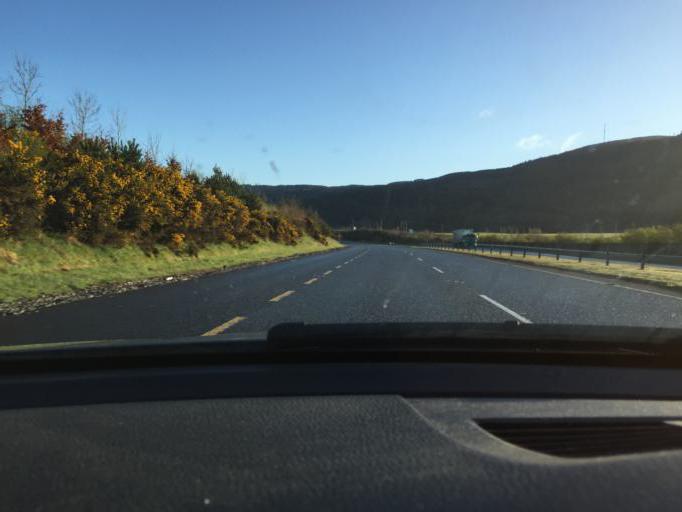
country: IE
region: Leinster
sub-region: Lu
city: Dundalk
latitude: 54.0625
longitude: -6.3543
